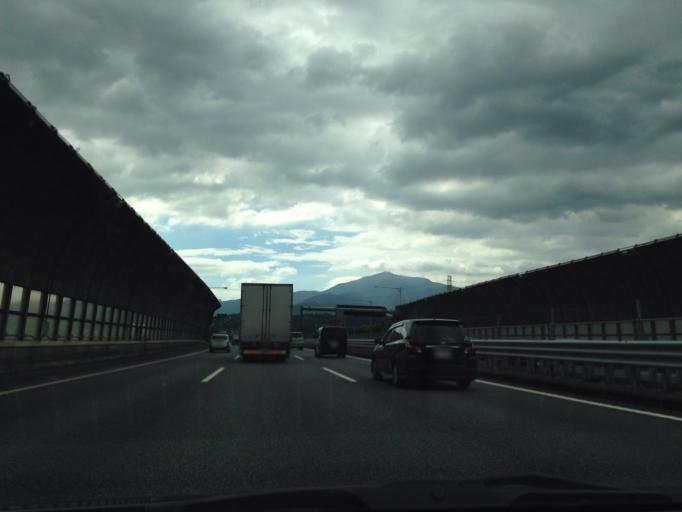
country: JP
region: Kanagawa
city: Atsugi
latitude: 35.4250
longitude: 139.3494
